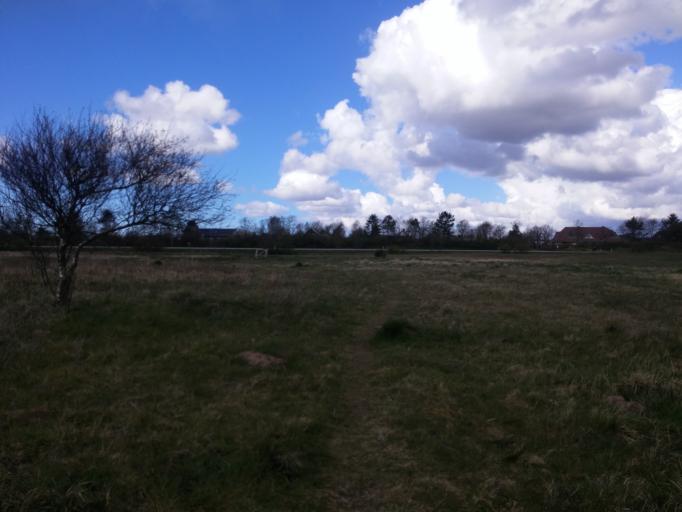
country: DK
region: Central Jutland
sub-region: Ringkobing-Skjern Kommune
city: Skjern
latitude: 55.9346
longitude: 8.5138
